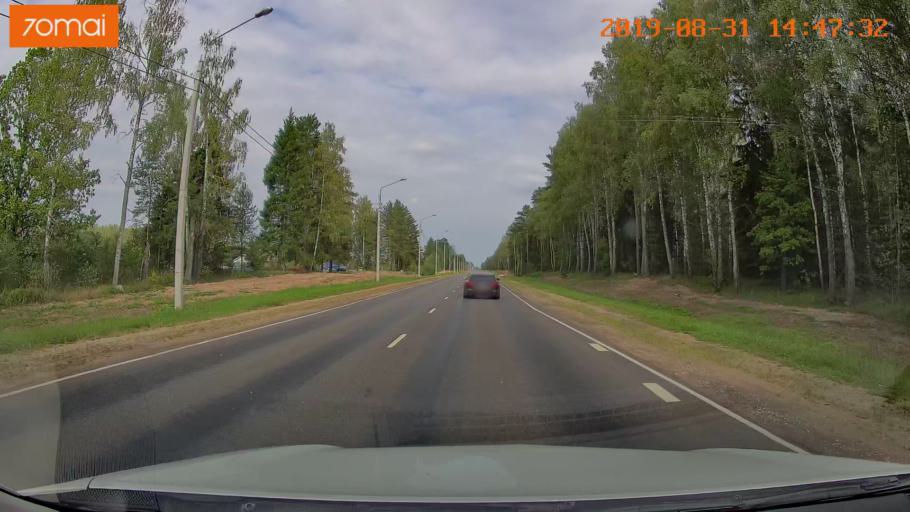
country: RU
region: Kaluga
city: Betlitsa
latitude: 54.2399
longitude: 33.7268
